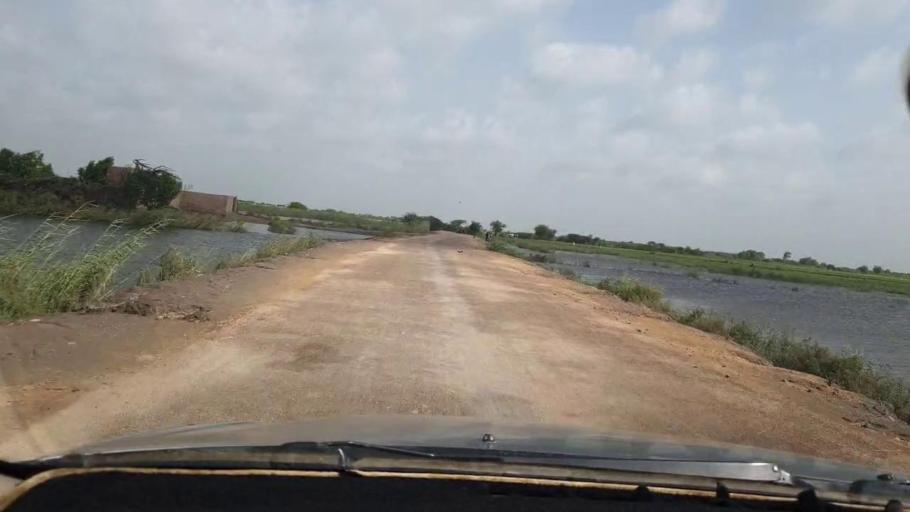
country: PK
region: Sindh
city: Tando Bago
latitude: 24.7882
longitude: 68.9799
